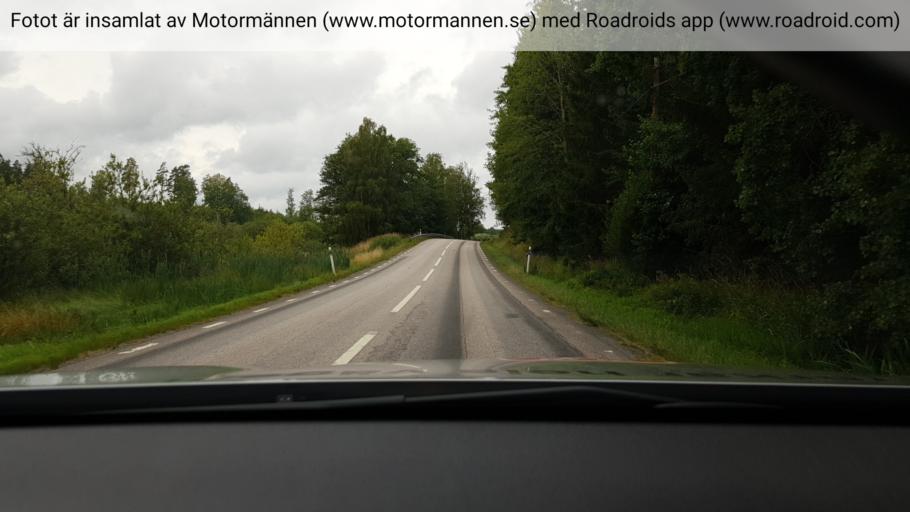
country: SE
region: Soedermanland
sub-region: Strangnas Kommun
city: Akers Styckebruk
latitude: 59.0853
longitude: 17.0805
